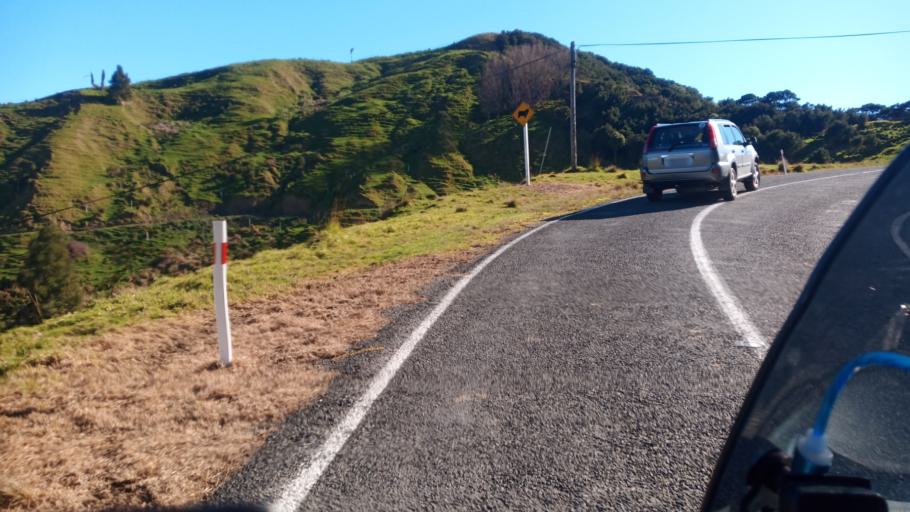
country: NZ
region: Gisborne
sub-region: Gisborne District
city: Gisborne
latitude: -38.2493
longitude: 178.3034
